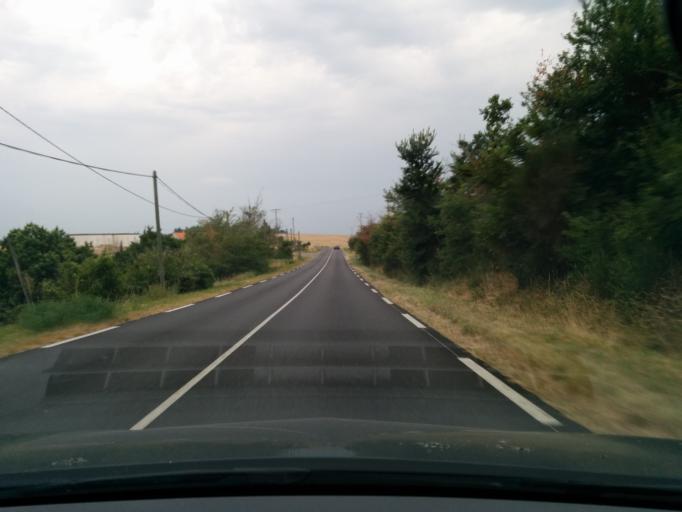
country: FR
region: Midi-Pyrenees
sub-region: Departement de la Haute-Garonne
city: Venerque
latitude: 43.4664
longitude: 1.4503
